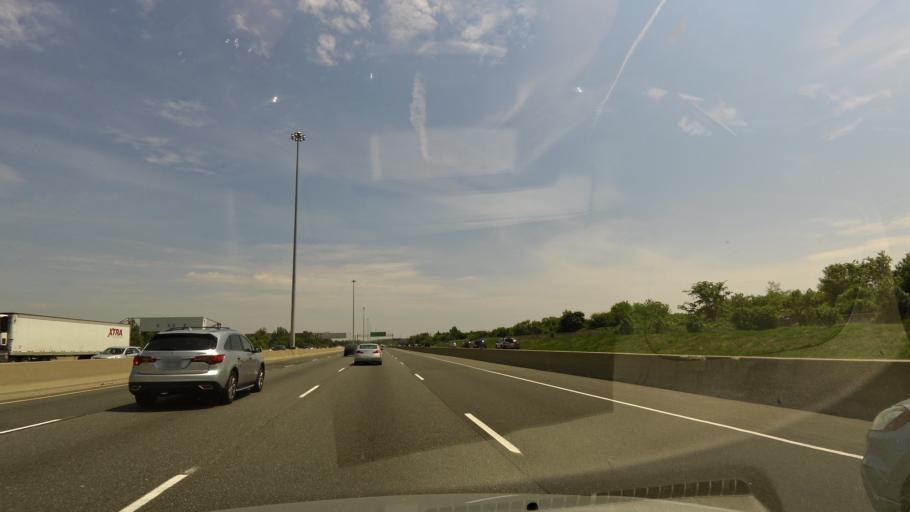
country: CA
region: Ontario
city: Scarborough
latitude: 43.7983
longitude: -79.1834
